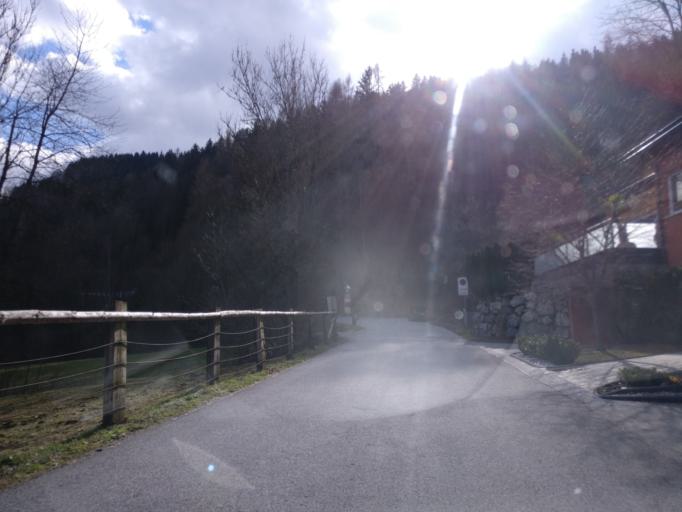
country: AT
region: Salzburg
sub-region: Politischer Bezirk Sankt Johann im Pongau
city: Bischofshofen
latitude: 47.4101
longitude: 13.2124
